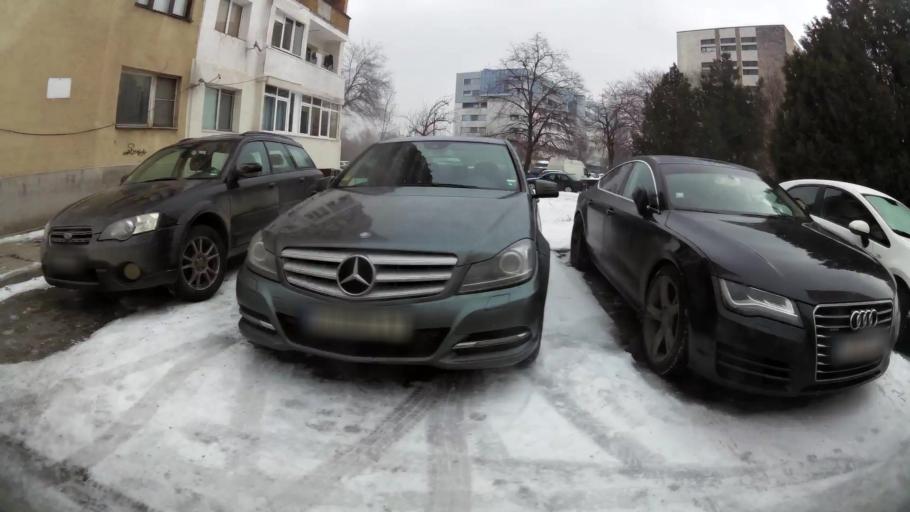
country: BG
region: Sofia-Capital
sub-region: Stolichna Obshtina
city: Sofia
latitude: 42.7175
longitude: 23.2915
